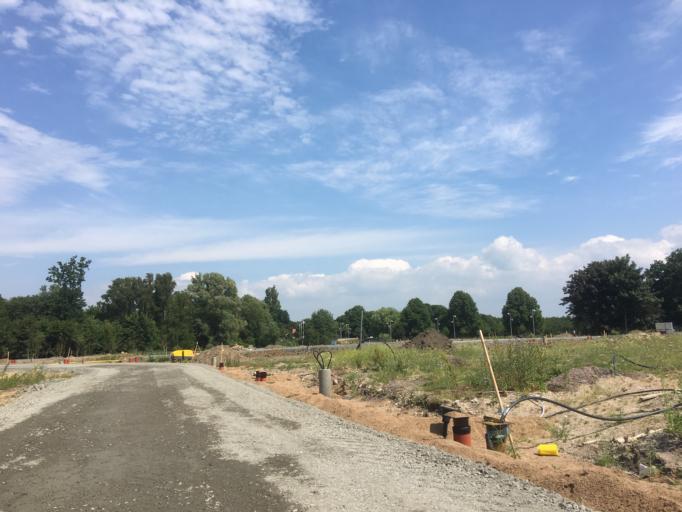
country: SE
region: Skane
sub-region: Landskrona
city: Landskrona
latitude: 55.9018
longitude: 12.8052
